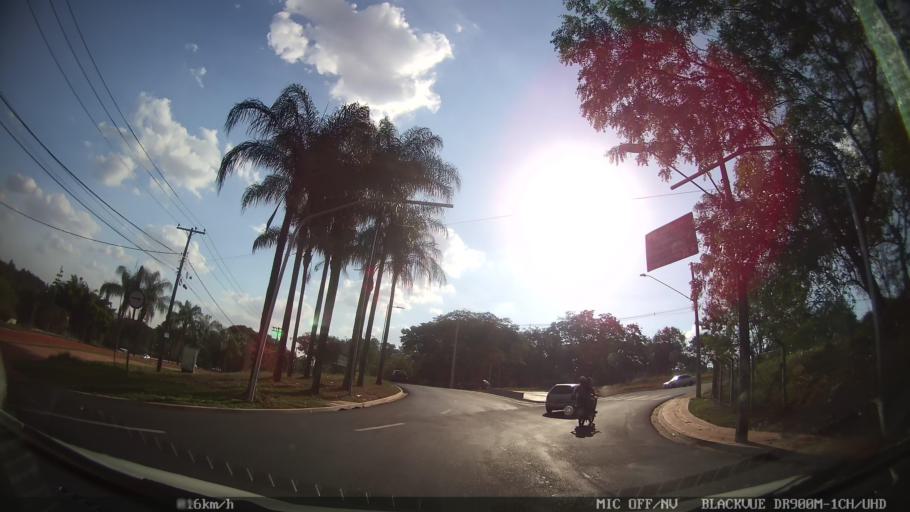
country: BR
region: Sao Paulo
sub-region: Ribeirao Preto
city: Ribeirao Preto
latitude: -21.1727
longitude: -47.8436
